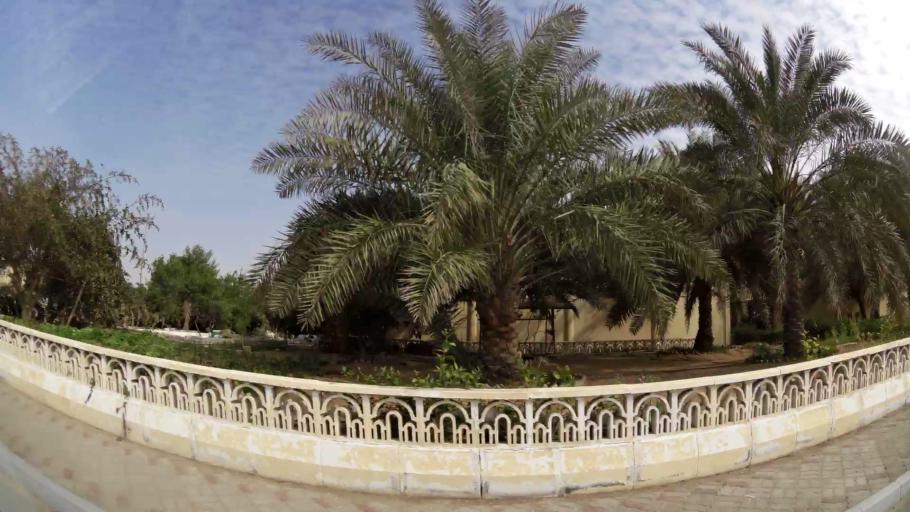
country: AE
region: Abu Dhabi
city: Abu Dhabi
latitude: 24.5967
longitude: 54.6951
